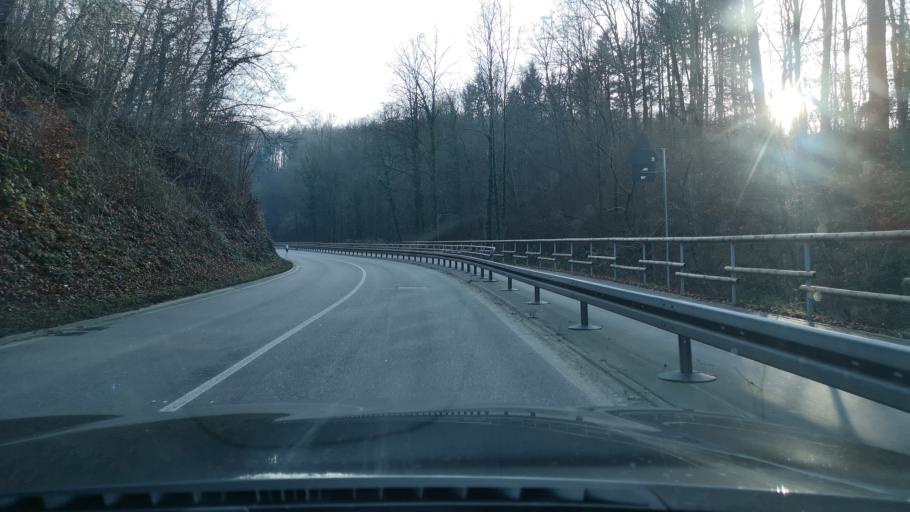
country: DE
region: Baden-Wuerttemberg
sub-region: Karlsruhe Region
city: Karlsruhe
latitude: 48.9798
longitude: 8.4652
